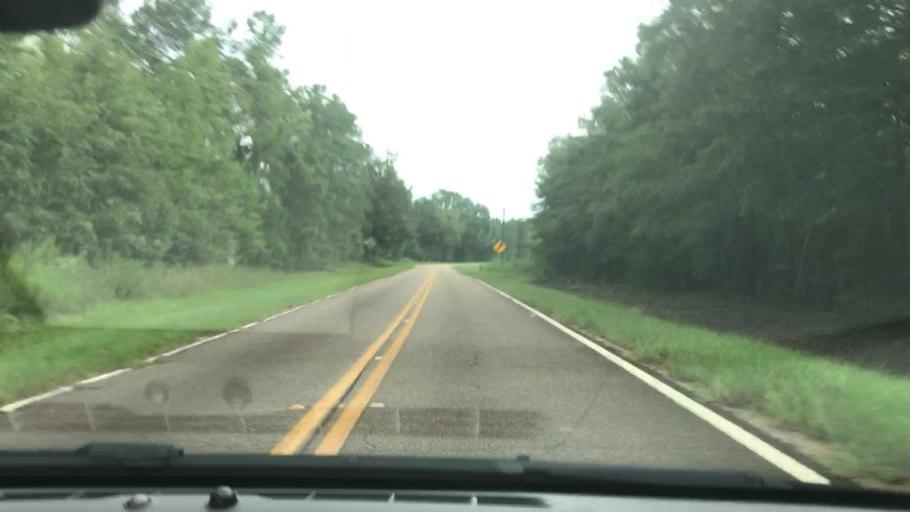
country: US
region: Georgia
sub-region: Stewart County
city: Lumpkin
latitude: 32.0461
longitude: -84.9062
